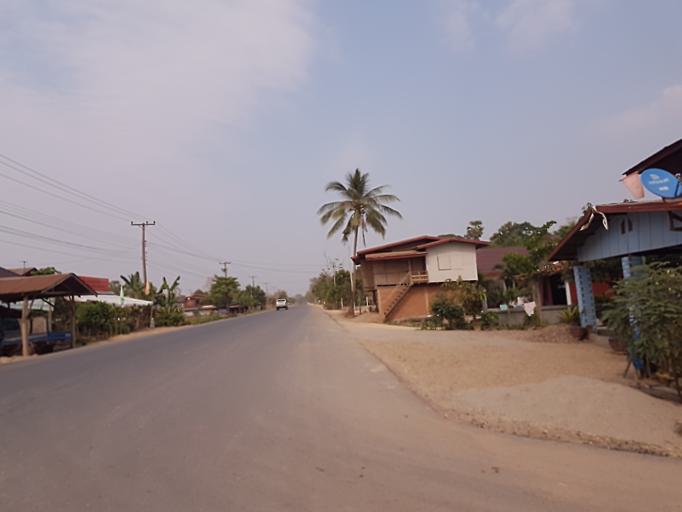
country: TH
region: Nong Khai
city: Nong Khai
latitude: 17.9561
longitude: 102.8282
